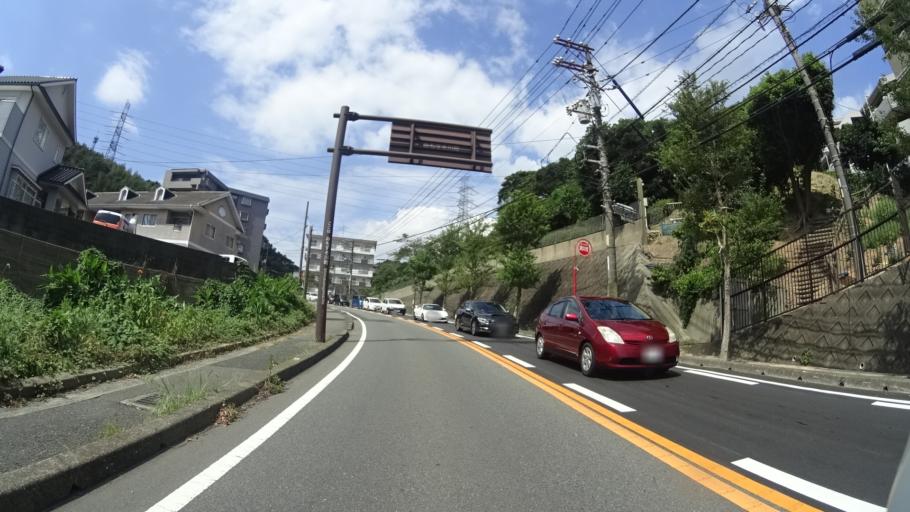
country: JP
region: Yamaguchi
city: Shimonoseki
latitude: 33.9686
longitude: 130.9545
